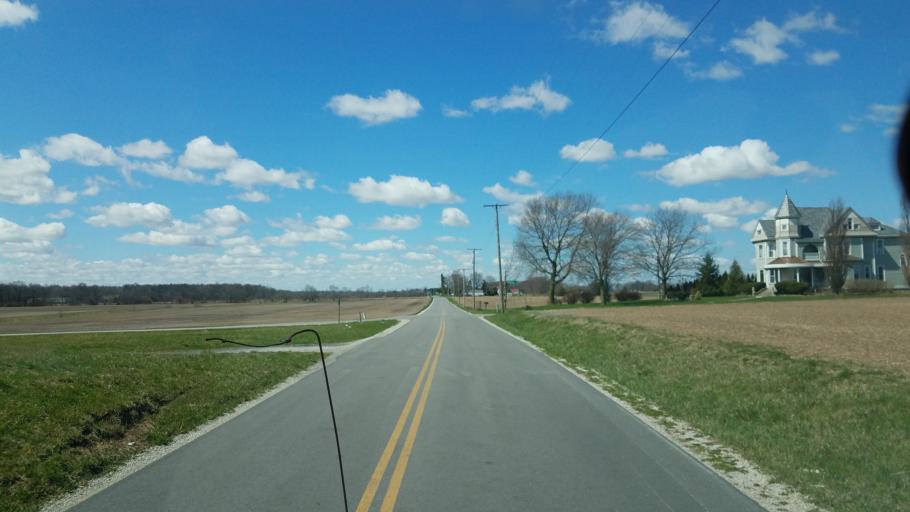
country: US
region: Ohio
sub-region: Seneca County
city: Fostoria
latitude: 41.1578
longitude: -83.4638
